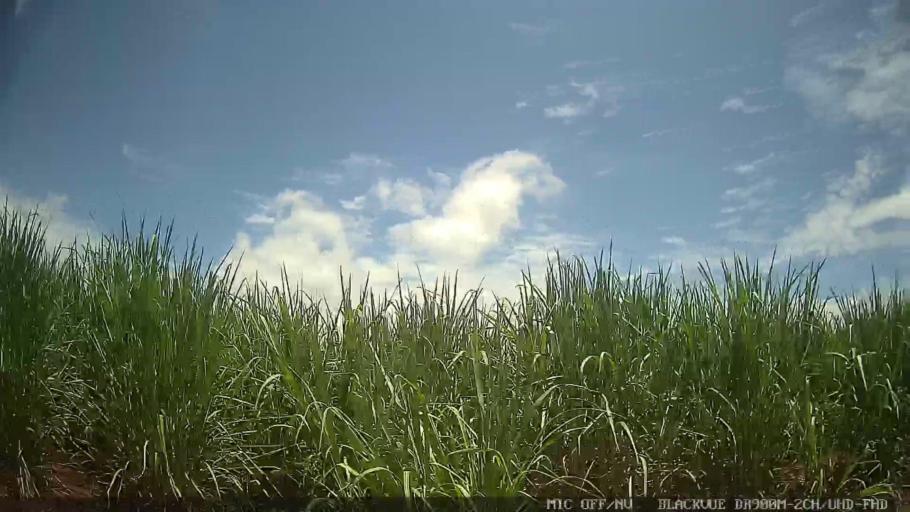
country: BR
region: Sao Paulo
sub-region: Laranjal Paulista
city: Laranjal Paulista
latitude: -23.0221
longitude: -47.8559
